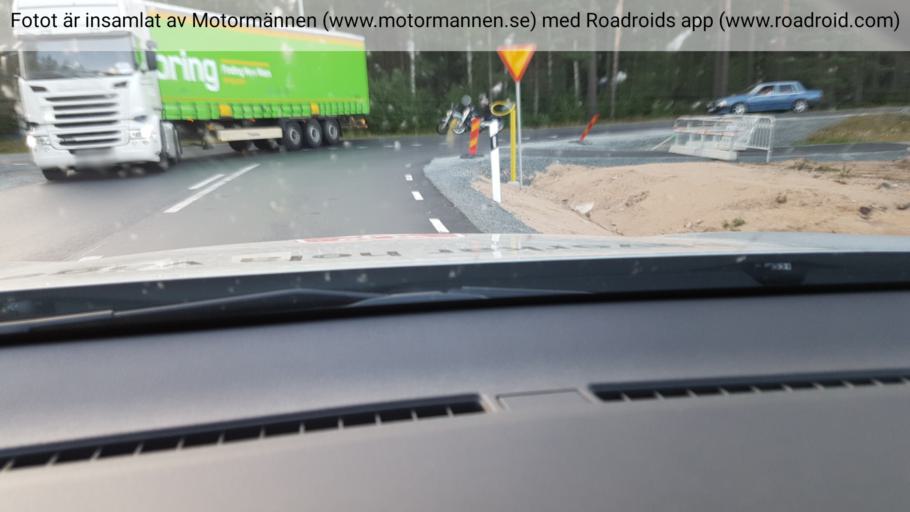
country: SE
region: Joenkoeping
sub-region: Mullsjo Kommun
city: Mullsjoe
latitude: 57.9031
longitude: 13.8589
